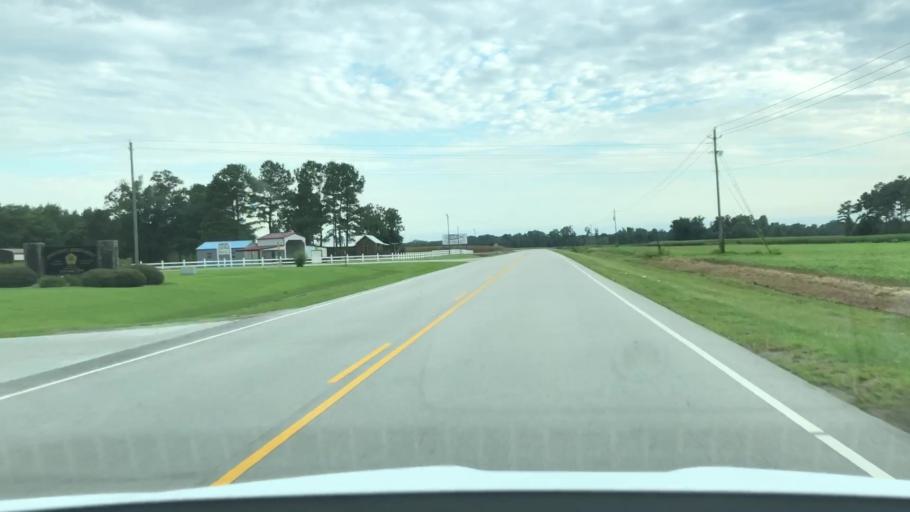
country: US
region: North Carolina
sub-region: Jones County
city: Trenton
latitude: 35.0450
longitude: -77.3515
